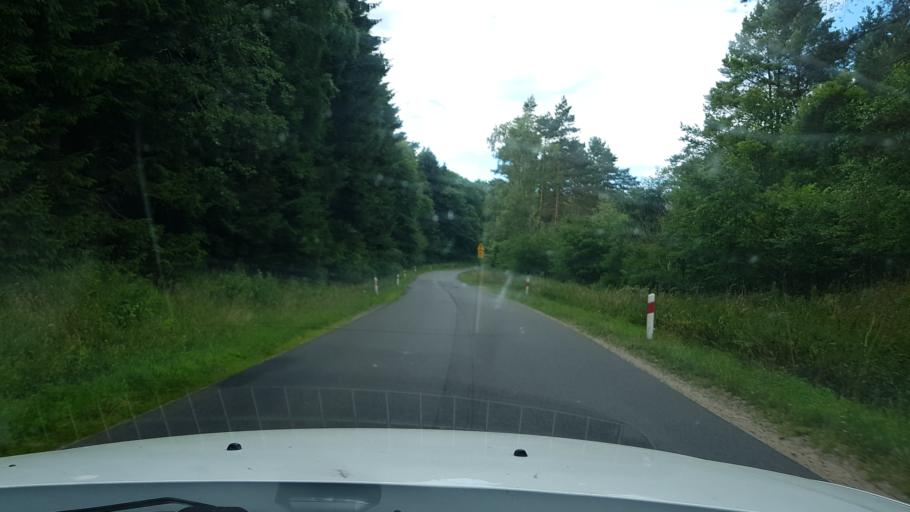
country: PL
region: West Pomeranian Voivodeship
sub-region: Powiat drawski
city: Zlocieniec
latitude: 53.4890
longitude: 16.0403
